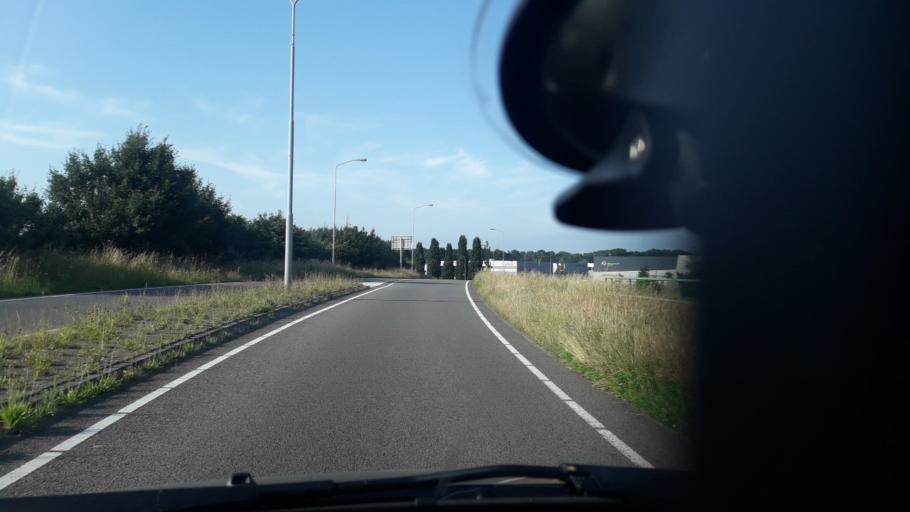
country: NL
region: Gelderland
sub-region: Gemeente Harderwijk
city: Harderwijk
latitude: 52.3240
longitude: 5.6105
